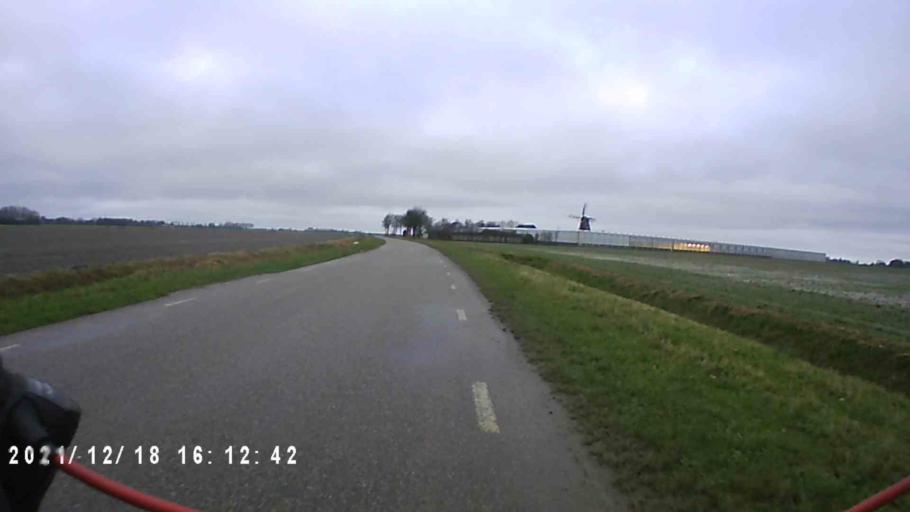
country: NL
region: Friesland
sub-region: Gemeente Dongeradeel
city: Anjum
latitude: 53.3661
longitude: 6.0687
